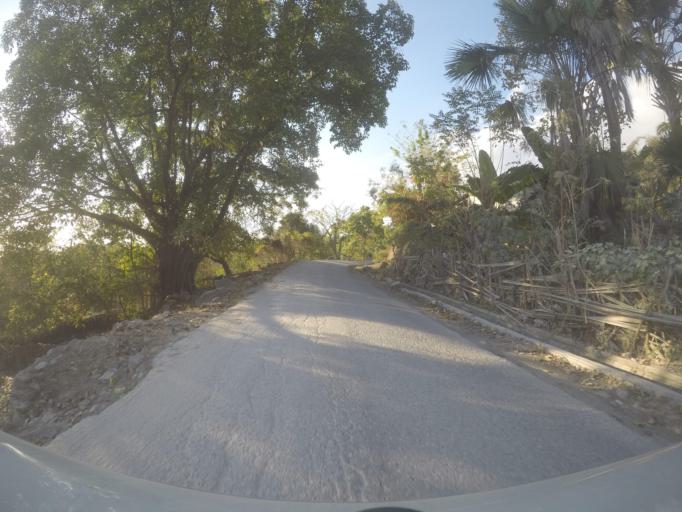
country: TL
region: Bobonaro
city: Maliana
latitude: -8.9619
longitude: 125.0291
